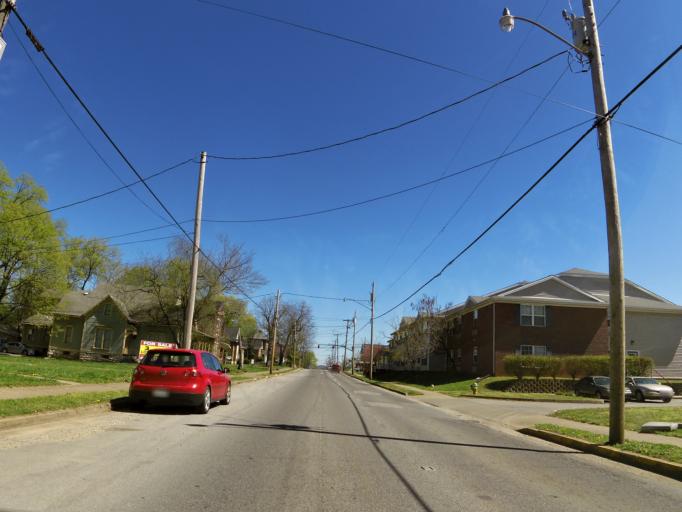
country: US
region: Kentucky
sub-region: Warren County
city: Bowling Green
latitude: 36.9920
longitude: -86.4497
